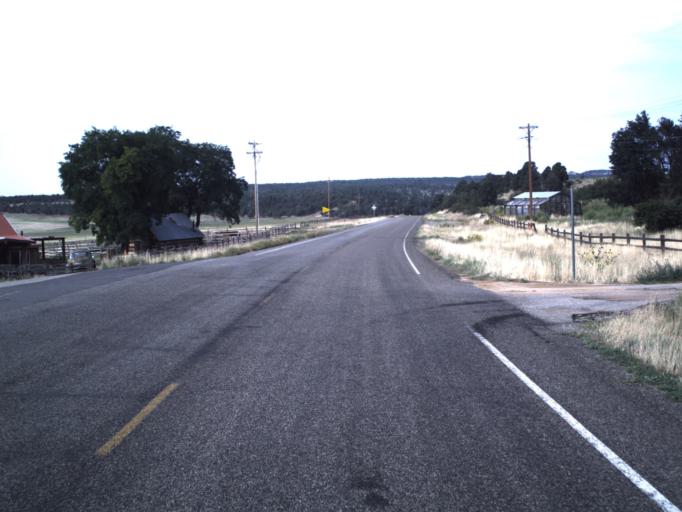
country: US
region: Utah
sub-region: Washington County
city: Hildale
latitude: 37.2475
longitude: -112.8031
